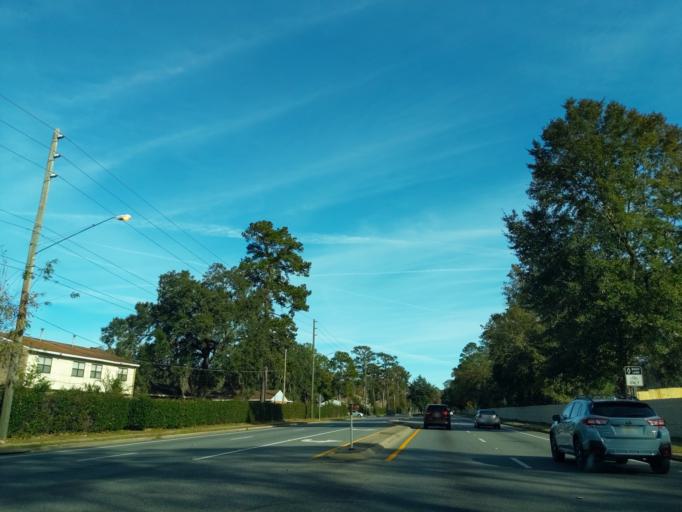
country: US
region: Florida
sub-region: Leon County
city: Tallahassee
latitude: 30.4126
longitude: -84.2703
